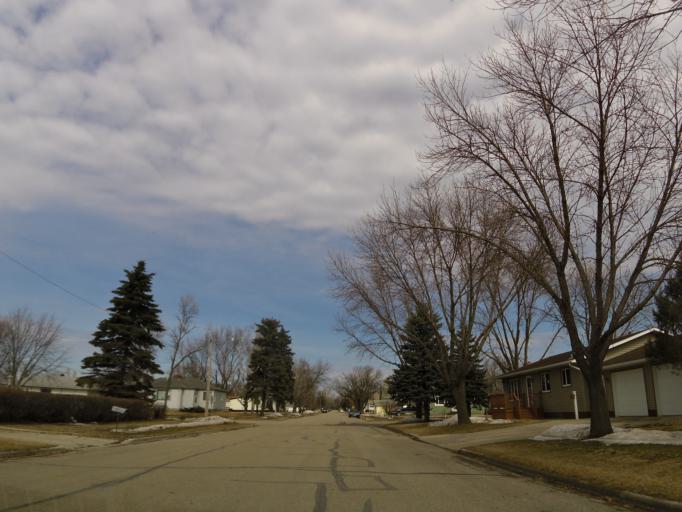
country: US
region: North Dakota
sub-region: Walsh County
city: Grafton
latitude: 48.2911
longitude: -97.3746
